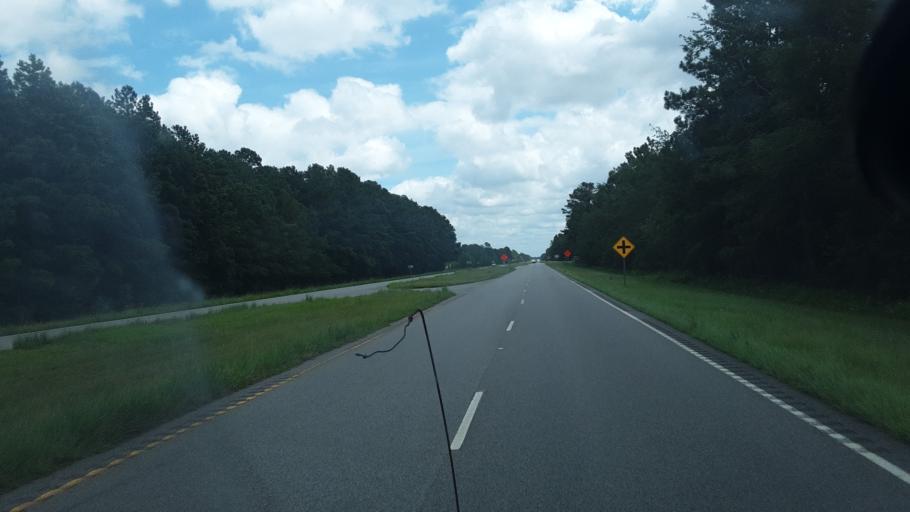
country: US
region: South Carolina
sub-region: Horry County
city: Loris
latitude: 34.0944
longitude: -78.9112
